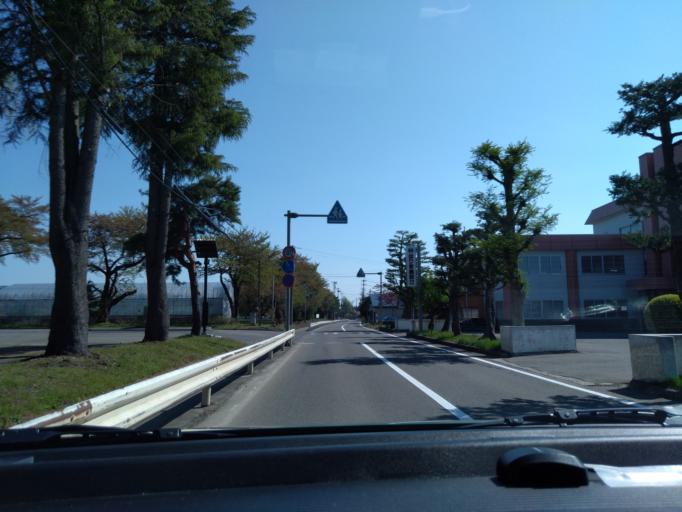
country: JP
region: Akita
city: Omagari
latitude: 39.4651
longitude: 140.5819
